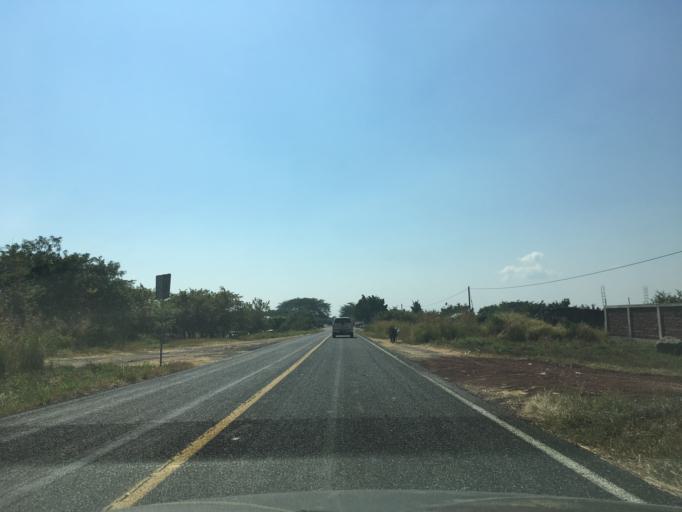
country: MX
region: Michoacan
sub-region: Gabriel Zamora
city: Lombardia
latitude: 19.2199
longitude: -102.0456
